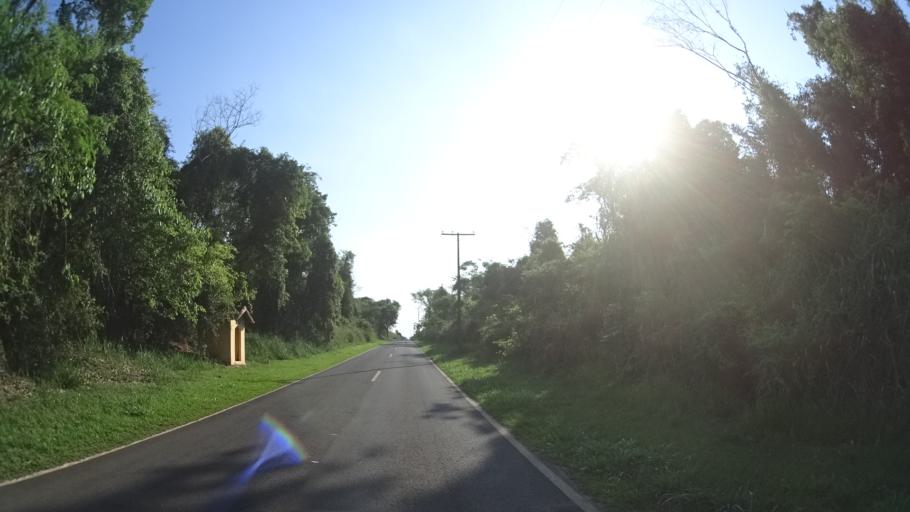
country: BR
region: Sao Paulo
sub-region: Urupes
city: Urupes
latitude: -21.3744
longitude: -49.4776
